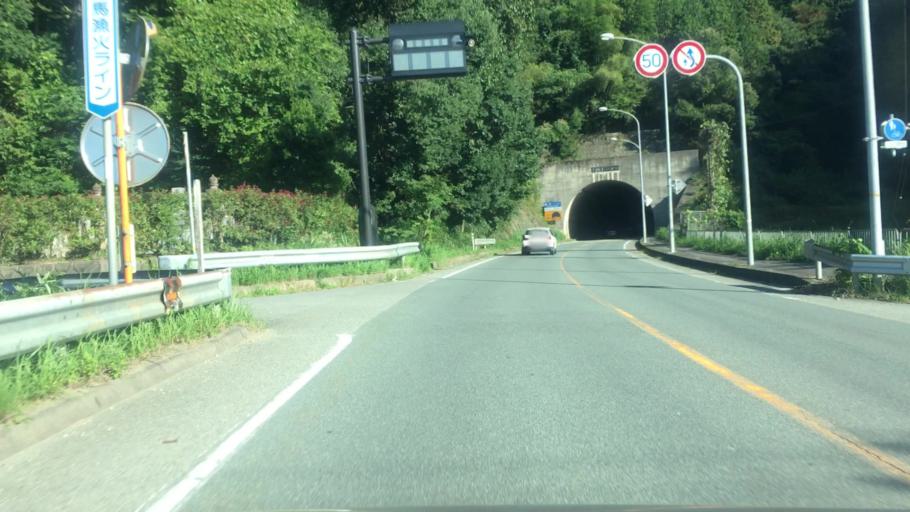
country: JP
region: Hyogo
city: Toyooka
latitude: 35.5589
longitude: 134.8273
